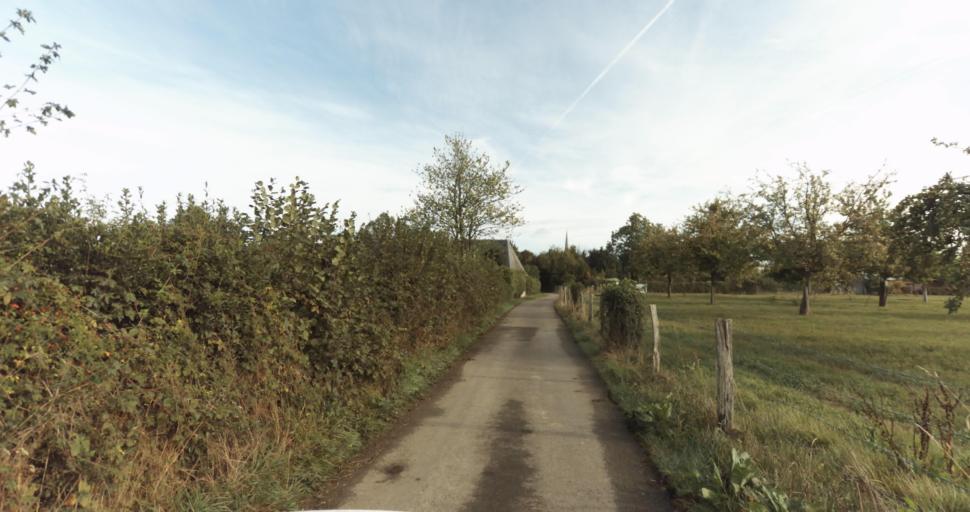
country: FR
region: Lower Normandy
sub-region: Departement de l'Orne
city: Vimoutiers
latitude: 48.9116
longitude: 0.3046
